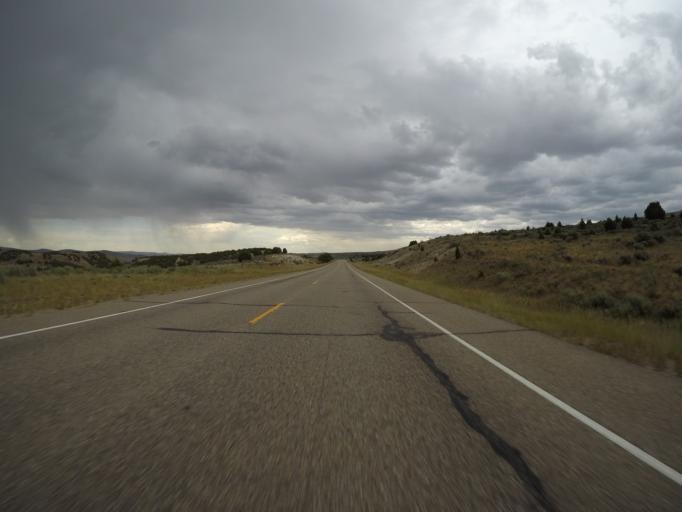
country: US
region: Colorado
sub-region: Rio Blanco County
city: Rangely
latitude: 40.3797
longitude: -108.3627
